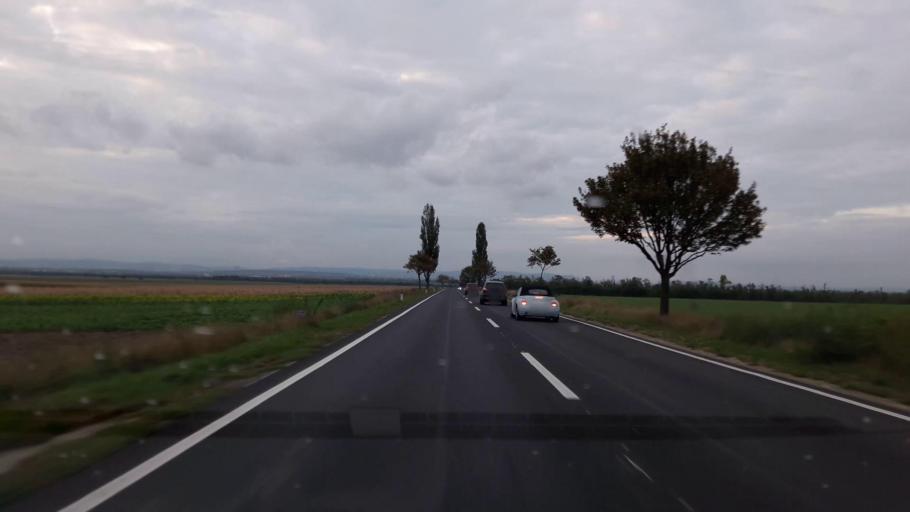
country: AT
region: Lower Austria
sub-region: Politischer Bezirk Wien-Umgebung
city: Rauchenwarth
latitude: 48.0955
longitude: 16.5447
